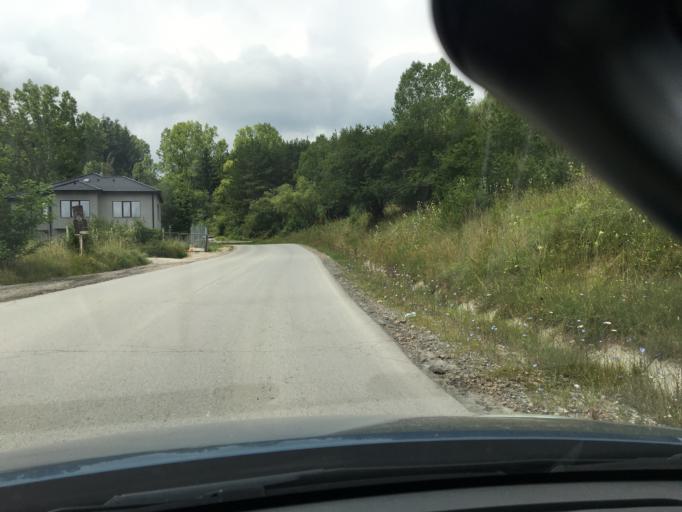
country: BG
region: Sofia-Capital
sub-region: Stolichna Obshtina
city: Sofia
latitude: 42.5964
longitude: 23.3652
